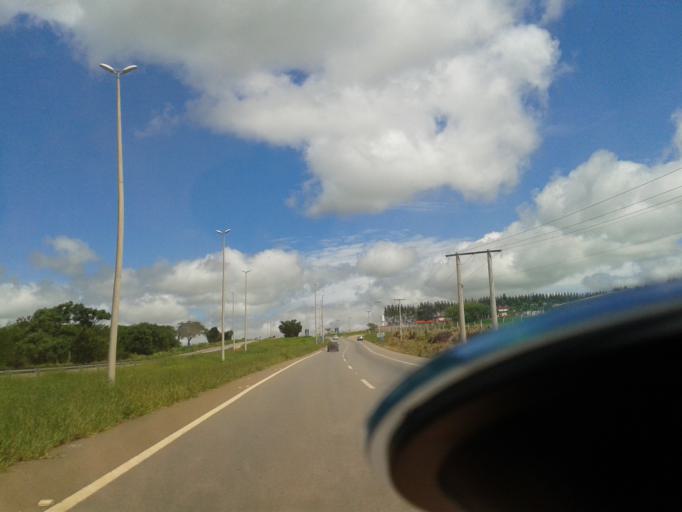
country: BR
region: Goias
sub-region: Goianira
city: Goianira
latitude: -16.4706
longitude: -49.4372
